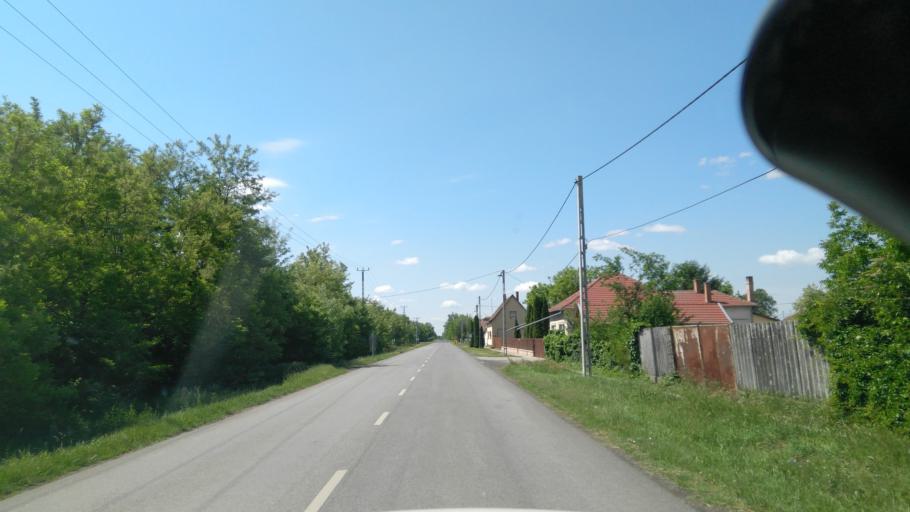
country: HU
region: Bekes
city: Medgyesegyhaza
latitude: 46.4888
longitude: 21.0258
